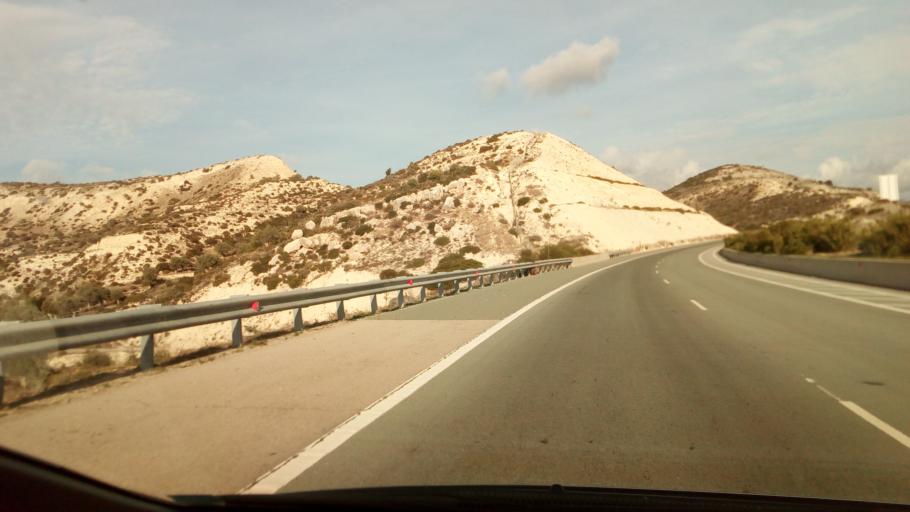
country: CY
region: Limassol
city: Pissouri
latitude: 34.6722
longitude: 32.6592
